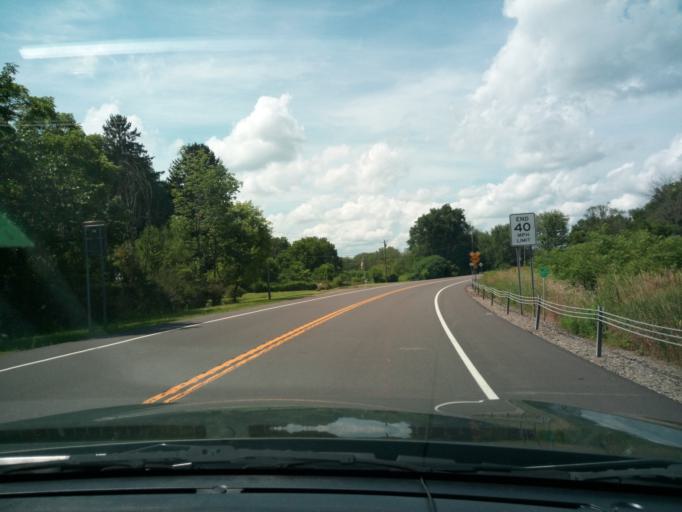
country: US
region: New York
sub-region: Chemung County
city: Southport
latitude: 42.0229
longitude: -76.7406
